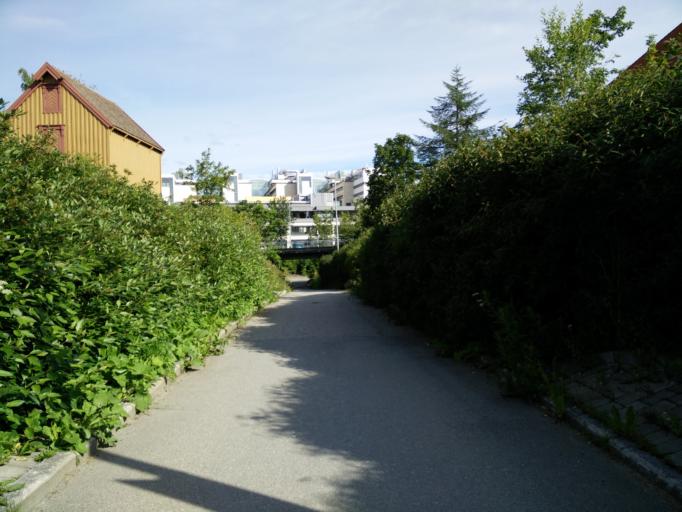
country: NO
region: Sor-Trondelag
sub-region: Trondheim
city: Trondheim
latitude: 63.4131
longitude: 10.4081
